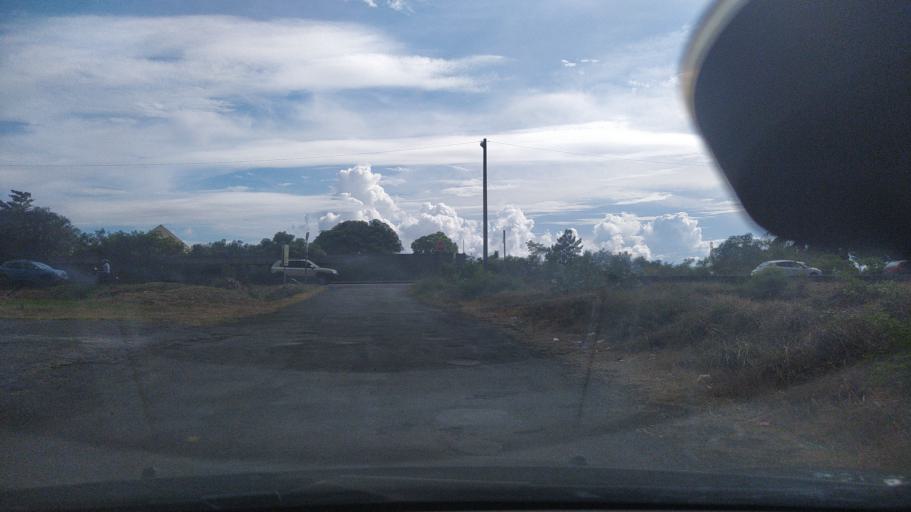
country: RE
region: Reunion
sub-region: Reunion
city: Saint-Pierre
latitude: -21.3106
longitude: 55.4721
